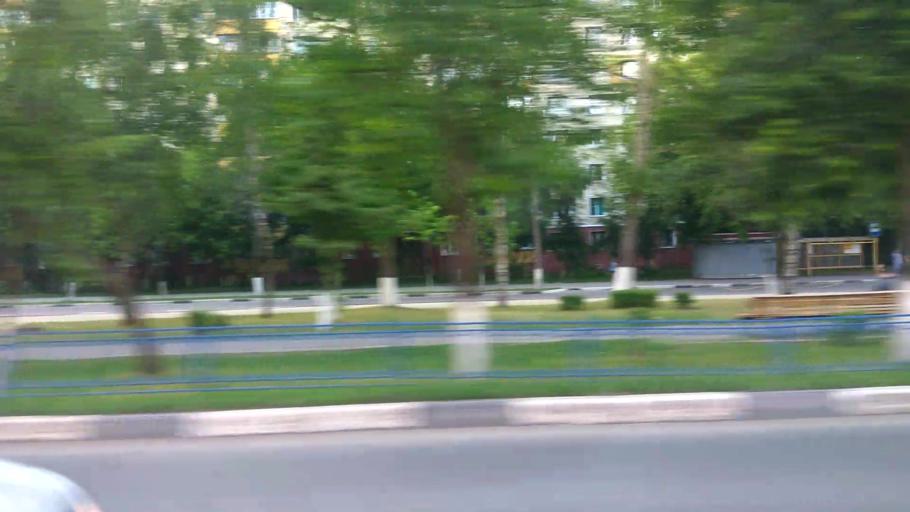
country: RU
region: Moskovskaya
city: Yubileyny
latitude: 55.9221
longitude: 37.8529
